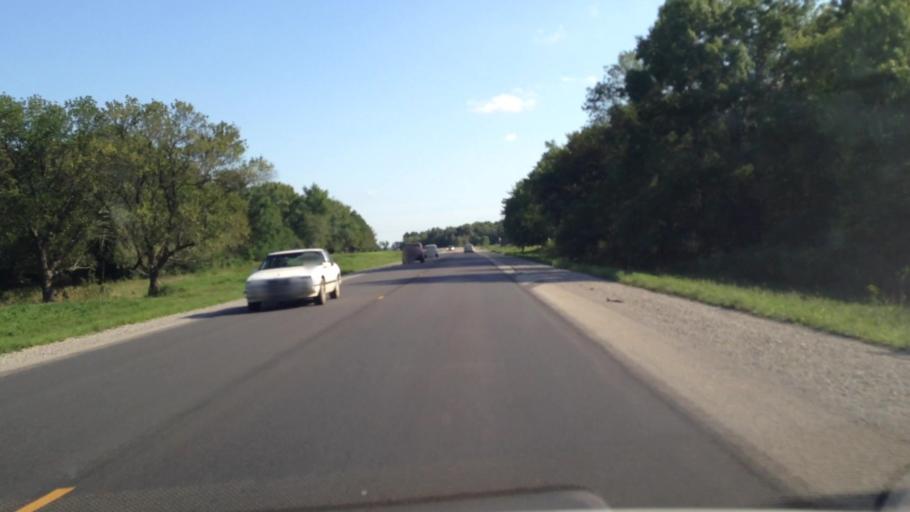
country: US
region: Kansas
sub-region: Crawford County
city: Arma
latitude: 37.5281
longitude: -94.7112
